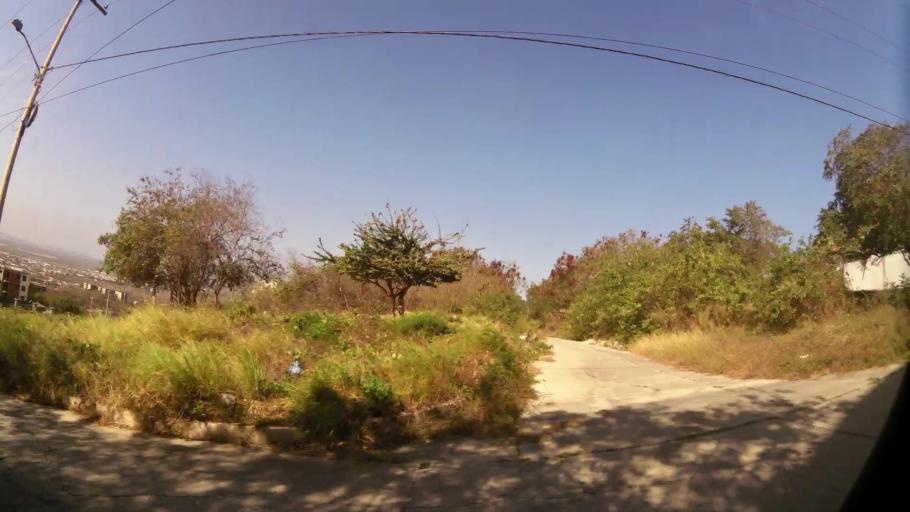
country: CO
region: Atlantico
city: Barranquilla
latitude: 10.9908
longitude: -74.8282
